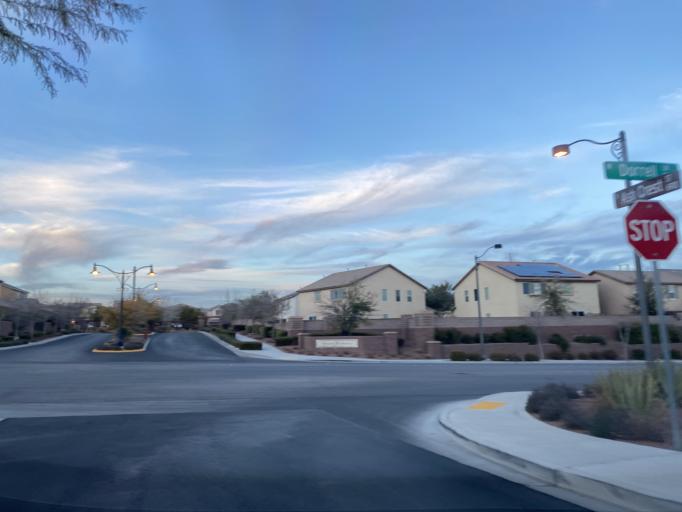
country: US
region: Nevada
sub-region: Clark County
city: Summerlin South
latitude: 36.2880
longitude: -115.3312
